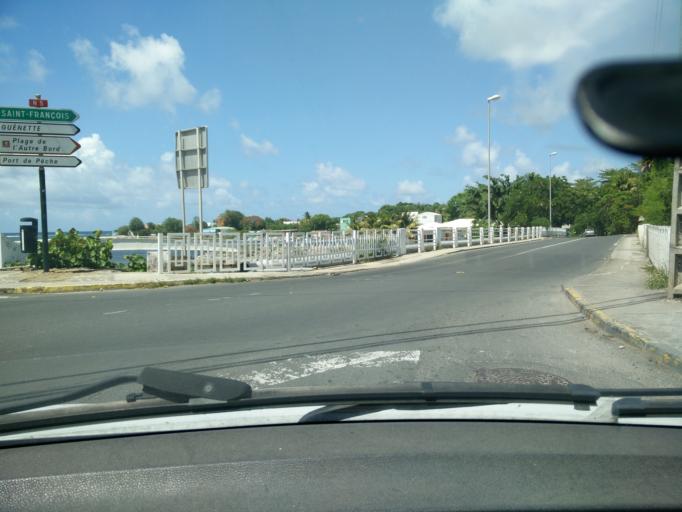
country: GP
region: Guadeloupe
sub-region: Guadeloupe
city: Le Moule
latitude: 16.3287
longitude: -61.3427
